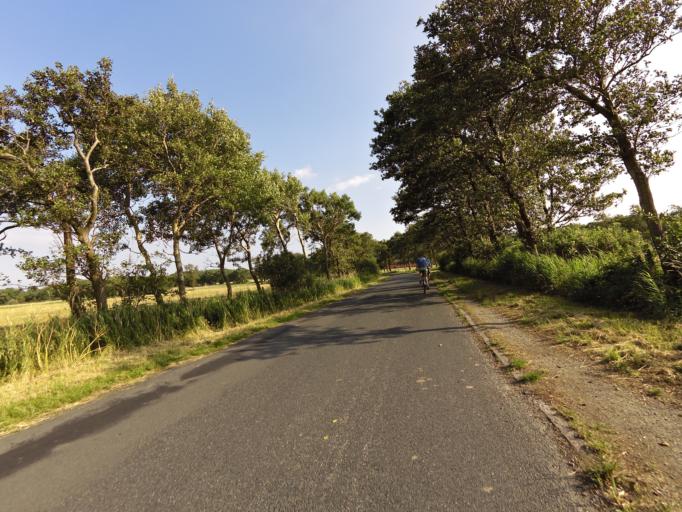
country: DE
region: Lower Saxony
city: Nordholz
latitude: 53.8299
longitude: 8.5813
